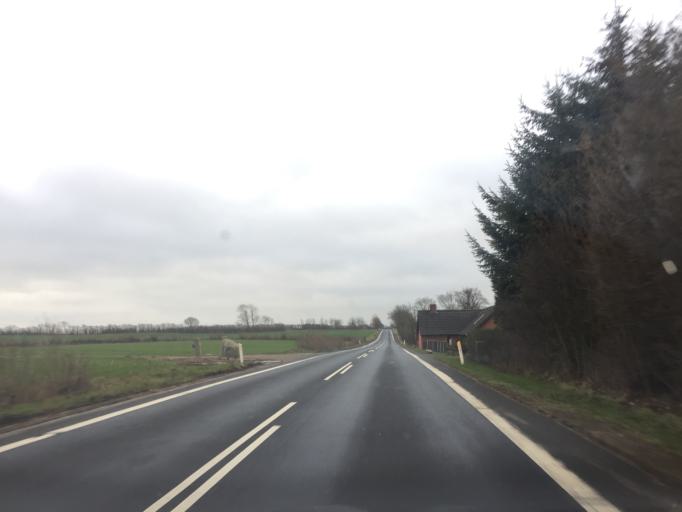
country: DK
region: South Denmark
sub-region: Svendborg Kommune
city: Thuro By
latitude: 55.1362
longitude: 10.6722
